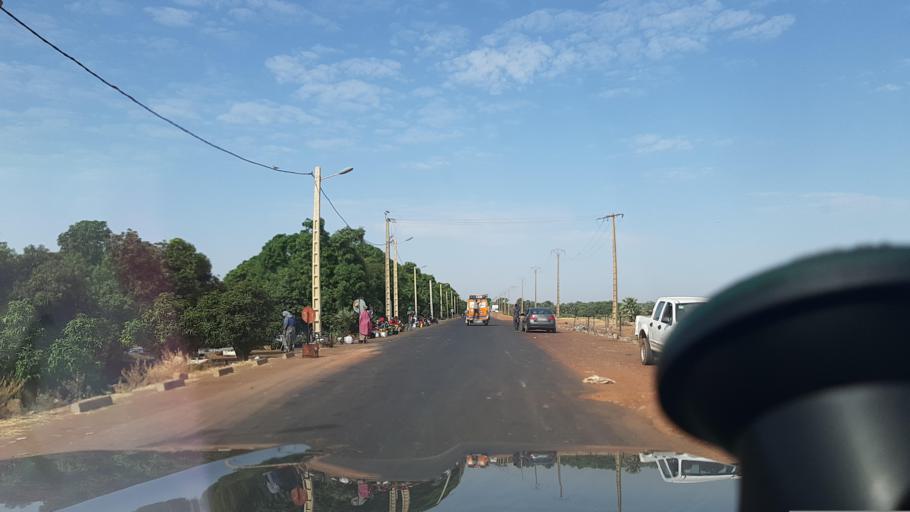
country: ML
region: Segou
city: Markala
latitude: 13.6814
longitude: -6.0851
